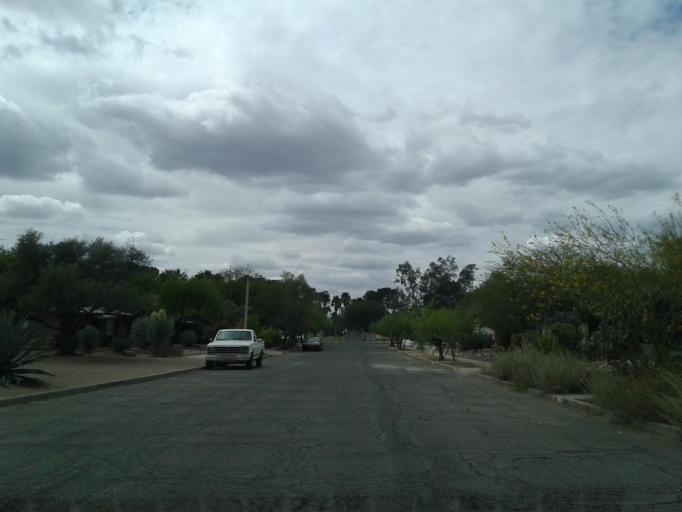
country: US
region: Arizona
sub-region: Pima County
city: Tucson
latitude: 32.2342
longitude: -110.9298
